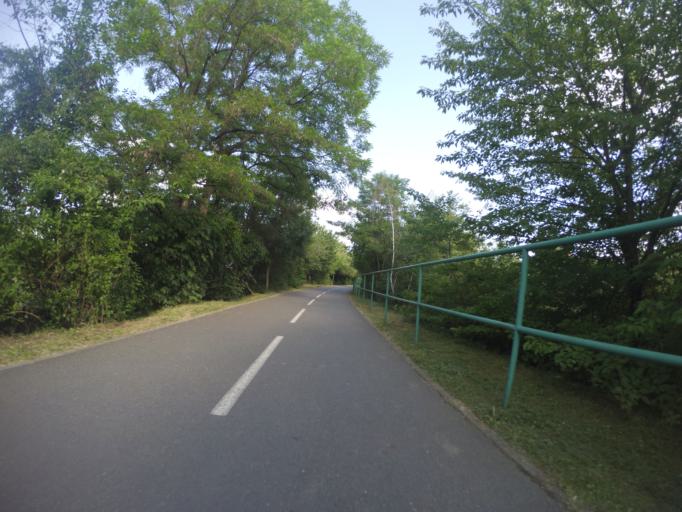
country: CZ
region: Praha
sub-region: Praha 9
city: Vysocany
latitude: 50.1060
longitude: 14.5265
